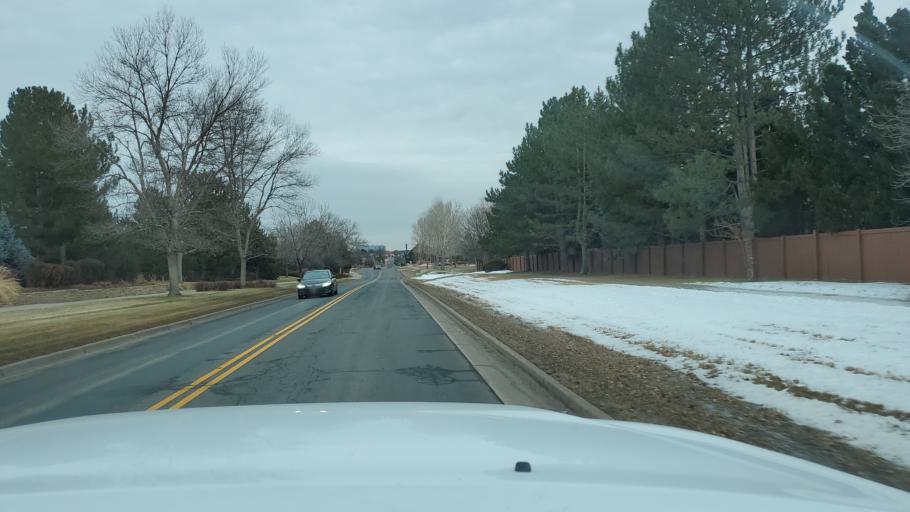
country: US
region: Colorado
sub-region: Arapahoe County
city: Greenwood Village
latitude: 39.6096
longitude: -104.9270
